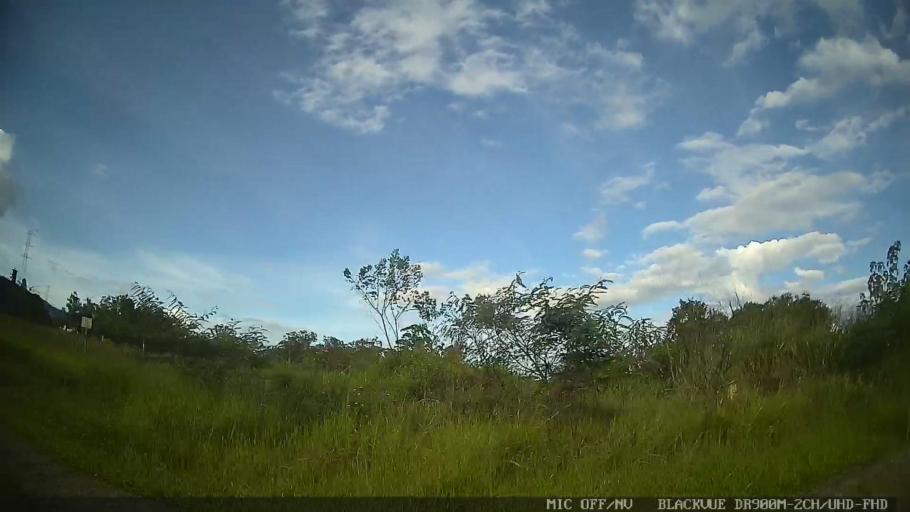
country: BR
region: Sao Paulo
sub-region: Mogi das Cruzes
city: Mogi das Cruzes
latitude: -23.5288
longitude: -46.1619
